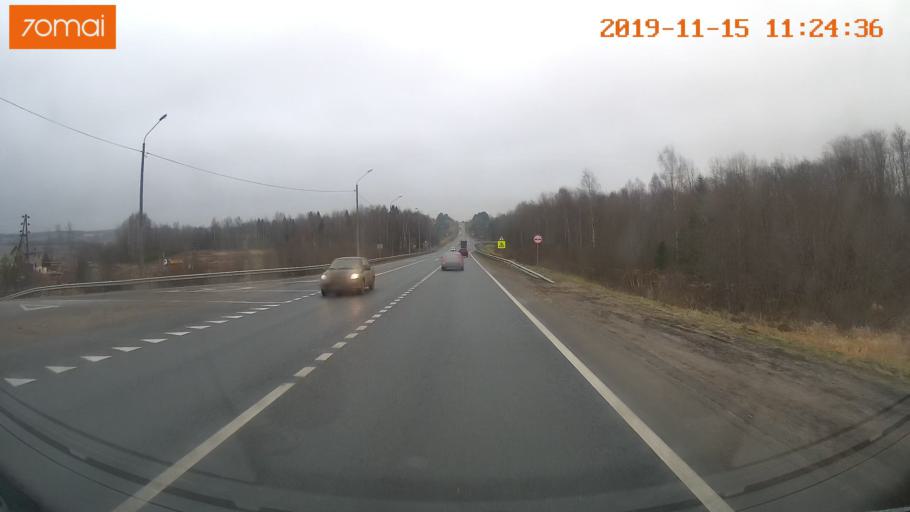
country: RU
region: Vologda
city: Molochnoye
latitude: 59.1580
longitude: 39.4084
